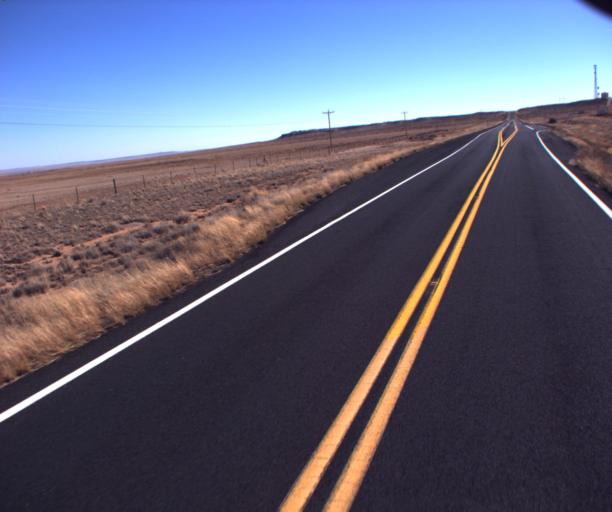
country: US
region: Arizona
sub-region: Coconino County
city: Tuba City
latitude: 35.9991
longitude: -111.0333
